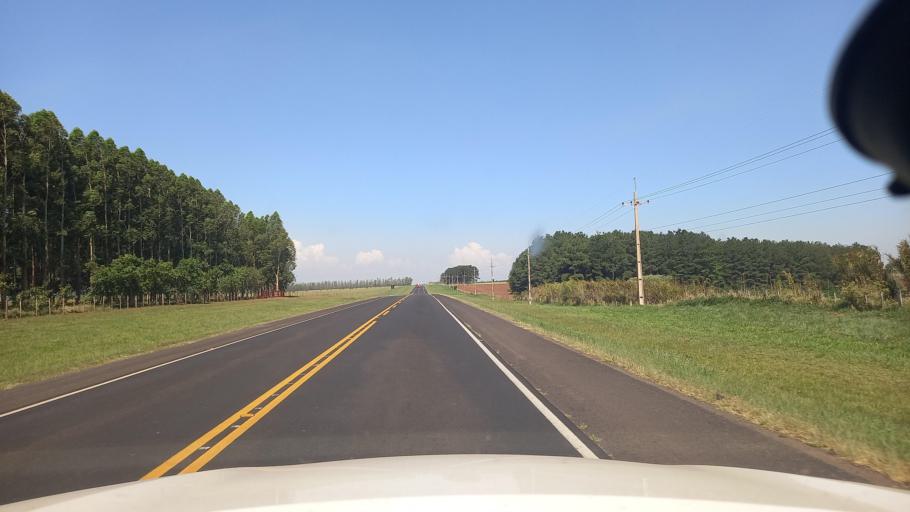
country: PY
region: Misiones
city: San Patricio
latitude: -26.9982
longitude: -56.7687
